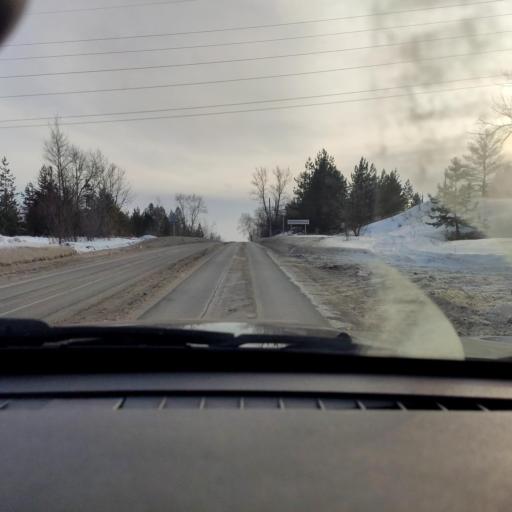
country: RU
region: Samara
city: Pribrezhnyy
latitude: 53.4982
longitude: 49.8485
